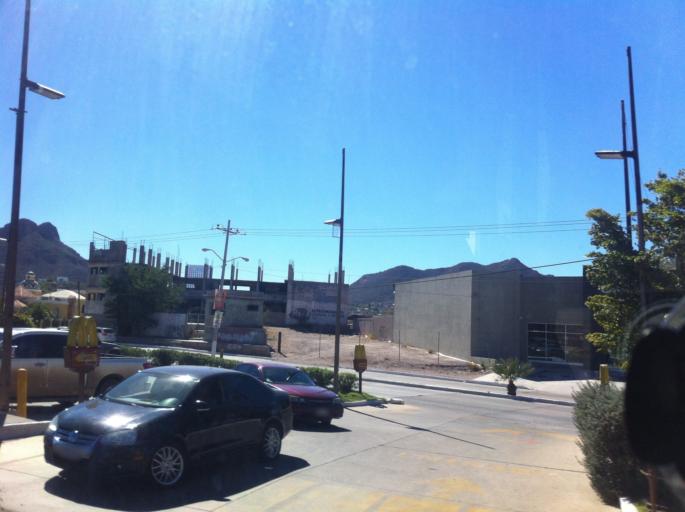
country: MX
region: Sonora
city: Heroica Guaymas
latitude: 27.9269
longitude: -110.9216
